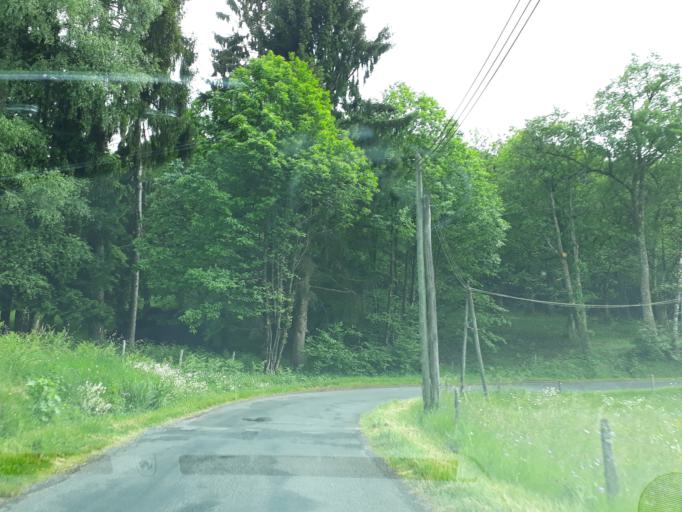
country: FR
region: Limousin
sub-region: Departement de la Correze
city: Beynat
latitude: 45.1182
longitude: 1.7606
